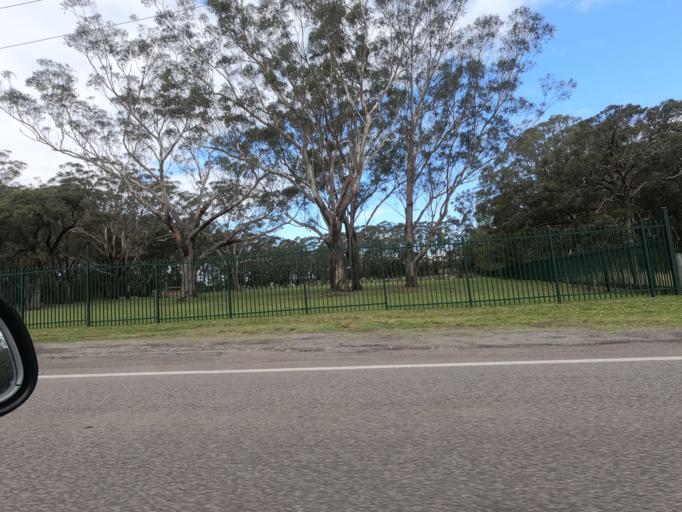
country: AU
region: New South Wales
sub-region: Wollongong
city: Dapto
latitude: -34.4715
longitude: 150.7935
